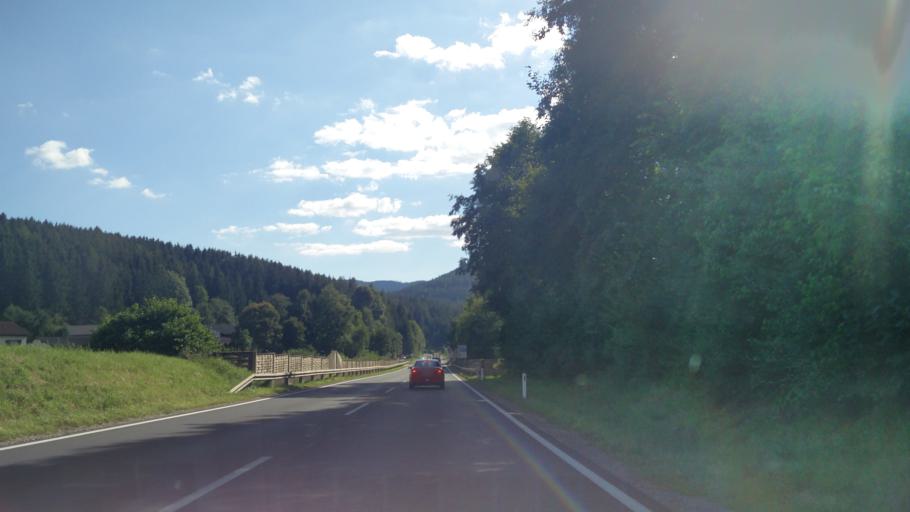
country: AT
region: Styria
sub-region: Politischer Bezirk Leoben
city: Trofaiach
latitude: 47.4063
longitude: 14.9985
